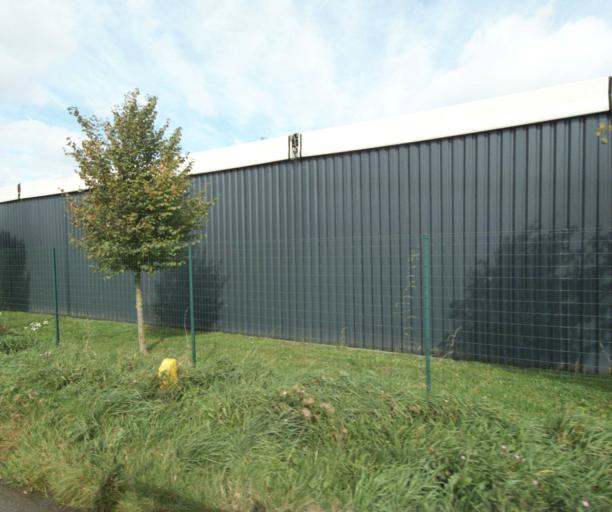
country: FR
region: Nord-Pas-de-Calais
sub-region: Departement du Nord
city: Houplines
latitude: 50.6781
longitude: 2.9056
